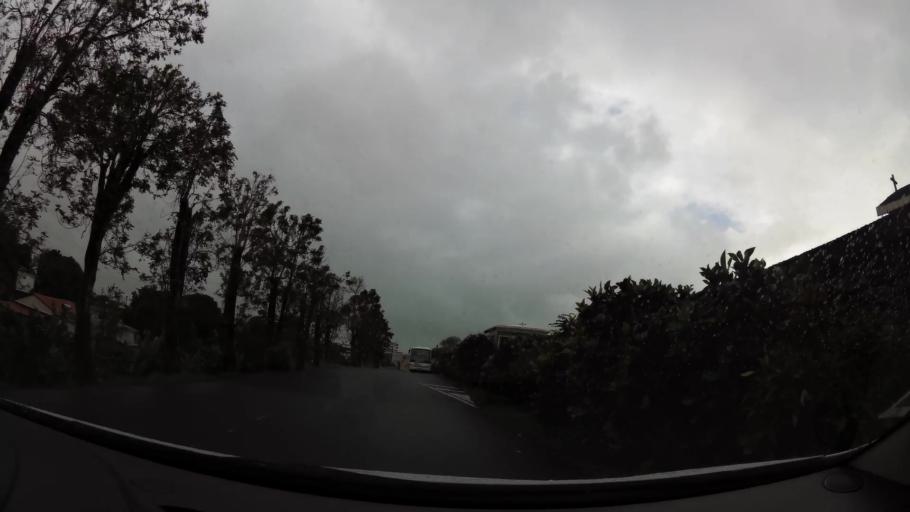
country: RE
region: Reunion
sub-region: Reunion
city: Saint-Andre
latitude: -20.9599
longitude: 55.6481
